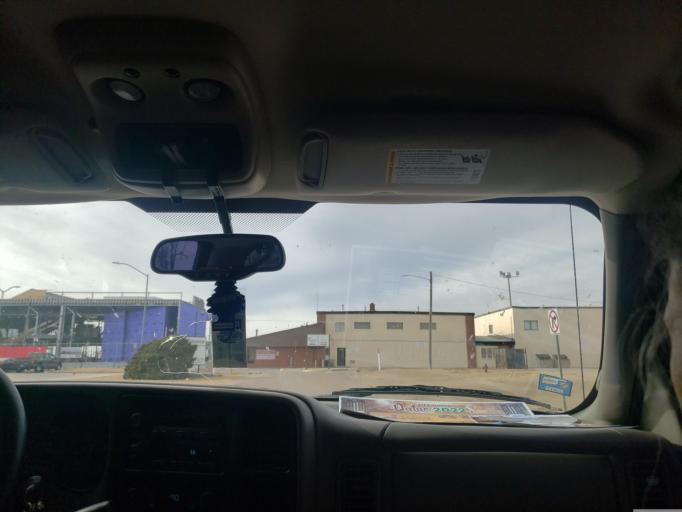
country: US
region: Kansas
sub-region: Finney County
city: Garden City
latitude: 37.9277
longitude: -100.7189
